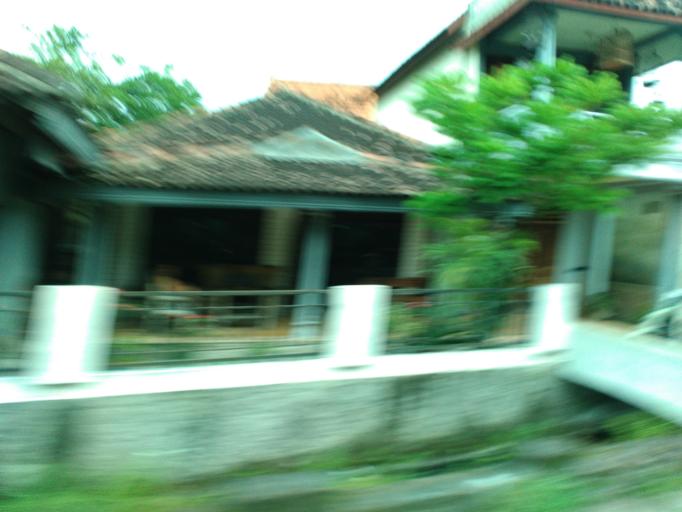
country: ID
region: Central Java
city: Delanggu
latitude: -7.6204
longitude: 110.7019
